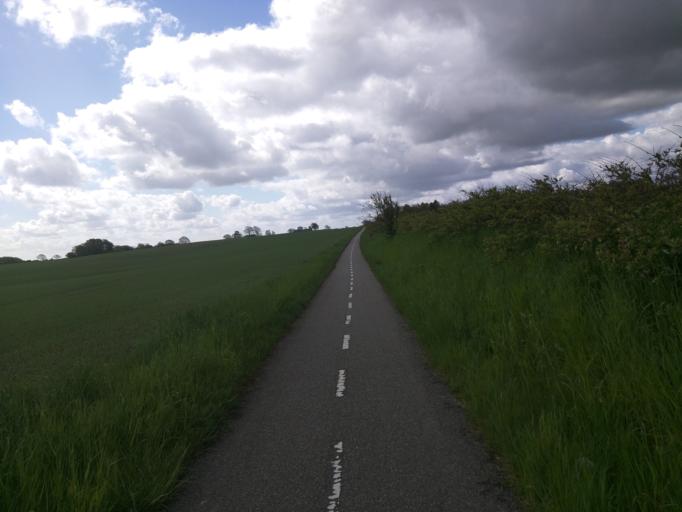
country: DK
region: Central Jutland
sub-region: Silkeborg Kommune
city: Kjellerup
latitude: 56.3112
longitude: 9.4226
